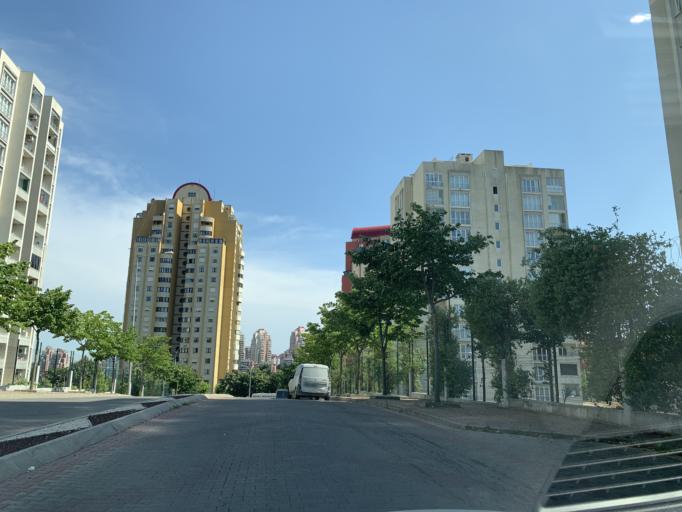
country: TR
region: Istanbul
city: Esenyurt
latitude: 41.0733
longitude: 28.6792
